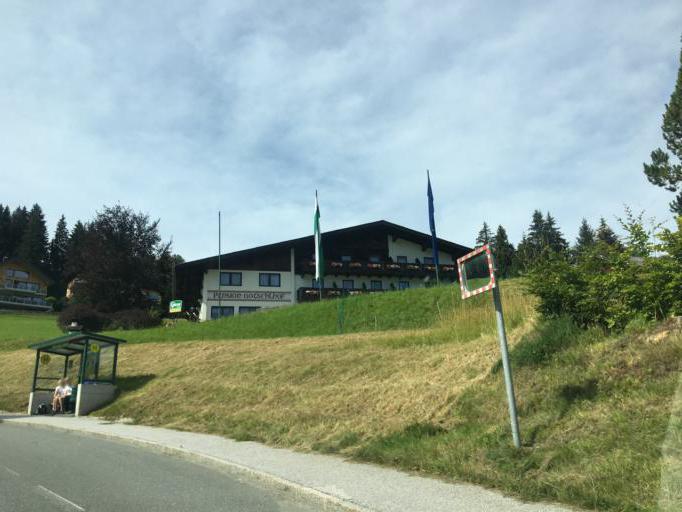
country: AT
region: Styria
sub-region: Politischer Bezirk Liezen
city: Schladming
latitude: 47.3872
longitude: 13.6786
